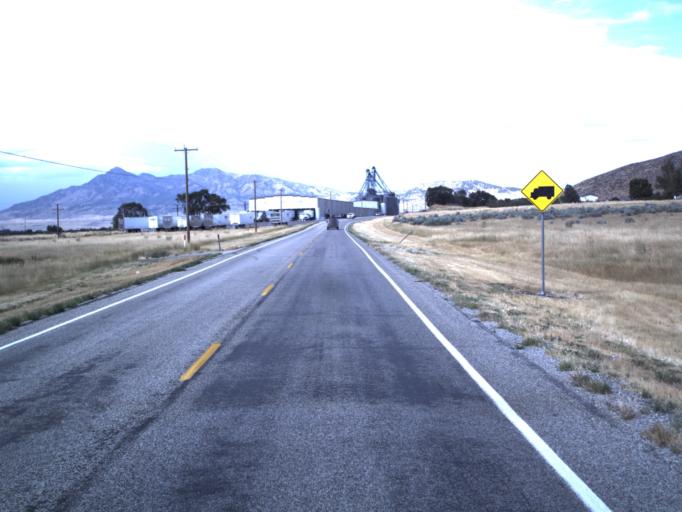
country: US
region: Utah
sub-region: Box Elder County
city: Garland
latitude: 41.7690
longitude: -112.0968
